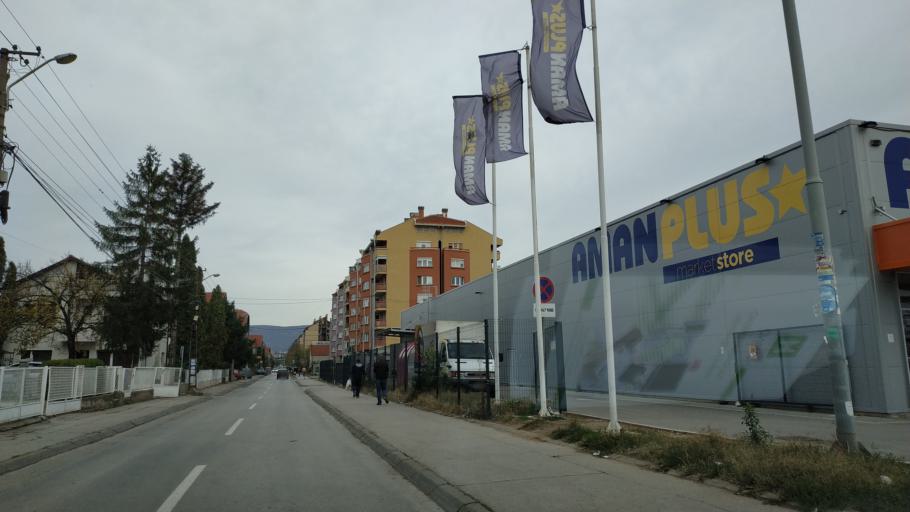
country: RS
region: Central Serbia
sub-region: Nisavski Okrug
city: Nis
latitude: 43.3133
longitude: 21.9338
